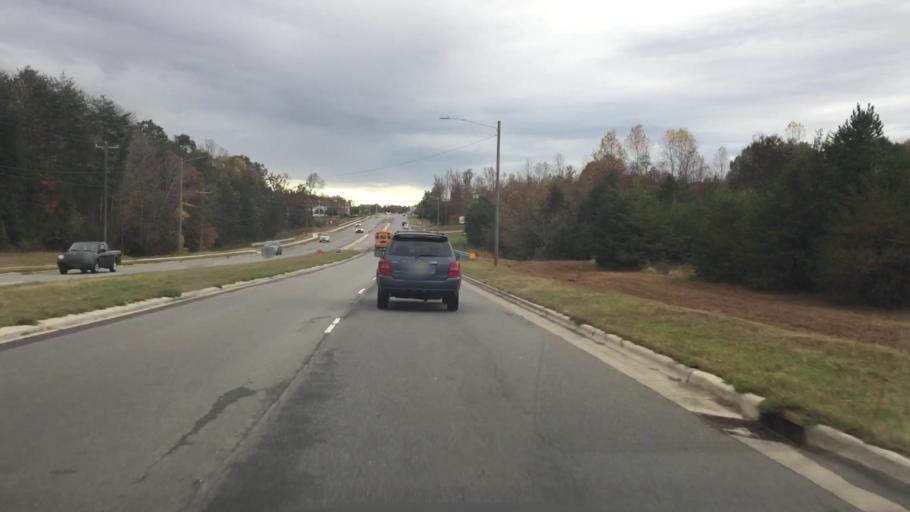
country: US
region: North Carolina
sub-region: Rockingham County
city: Reidsville
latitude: 36.3478
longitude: -79.6930
